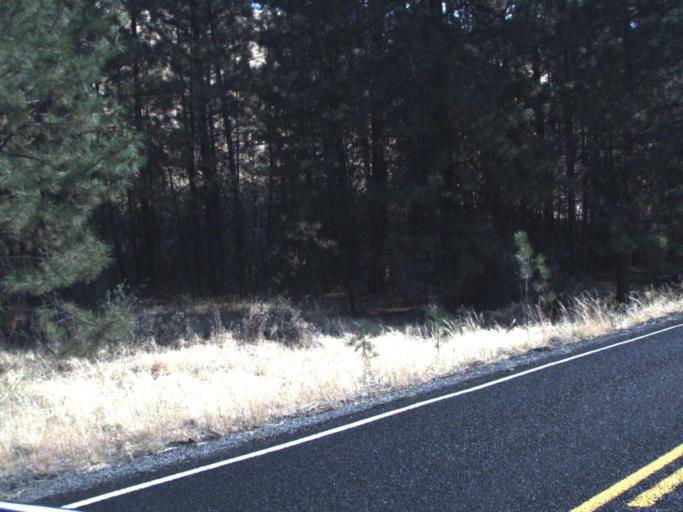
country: US
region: Washington
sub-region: Spokane County
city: Fairchild Air Force Base
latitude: 47.8390
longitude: -117.7701
